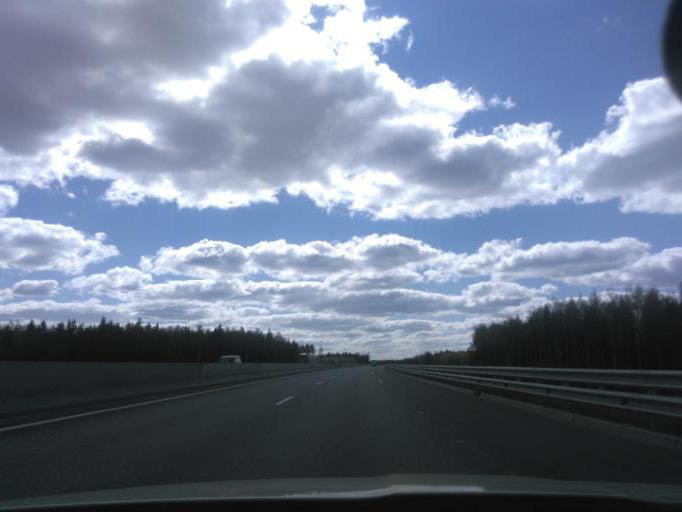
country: RU
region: Moskovskaya
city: Mendeleyevo
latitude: 56.0852
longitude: 37.2057
